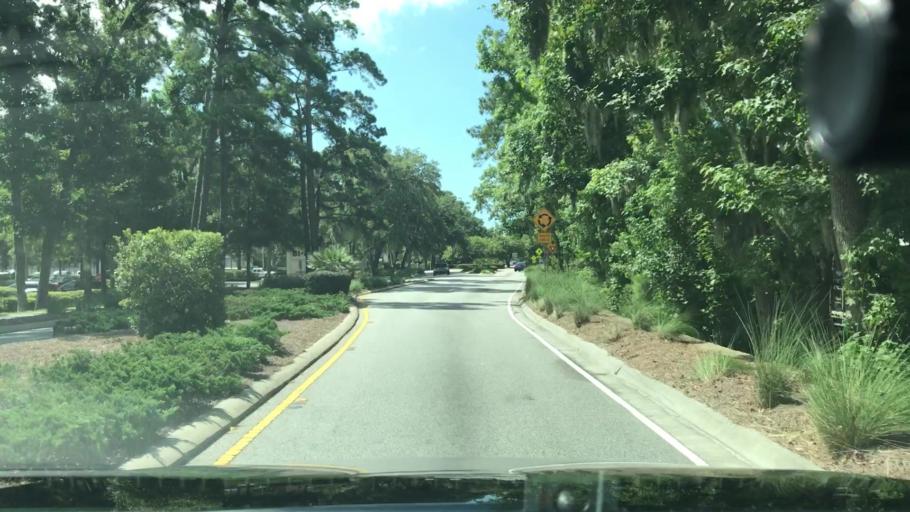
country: US
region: South Carolina
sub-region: Beaufort County
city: Hilton Head Island
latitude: 32.2135
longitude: -80.7027
